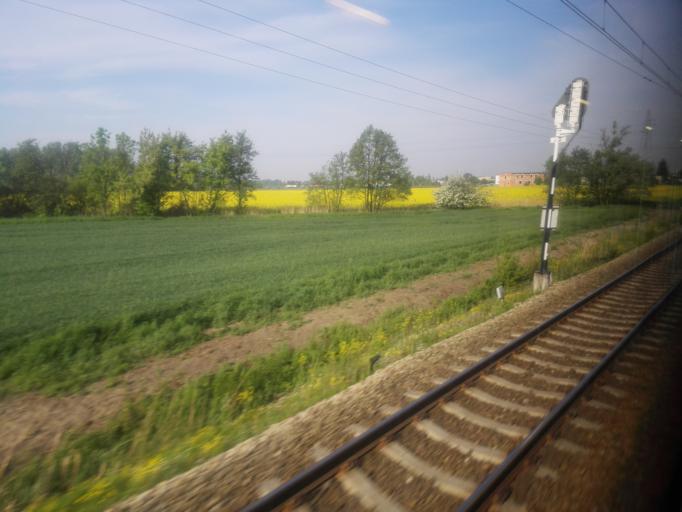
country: PL
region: Greater Poland Voivodeship
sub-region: Powiat wrzesinski
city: Wrzesnia
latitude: 52.3360
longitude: 17.6036
